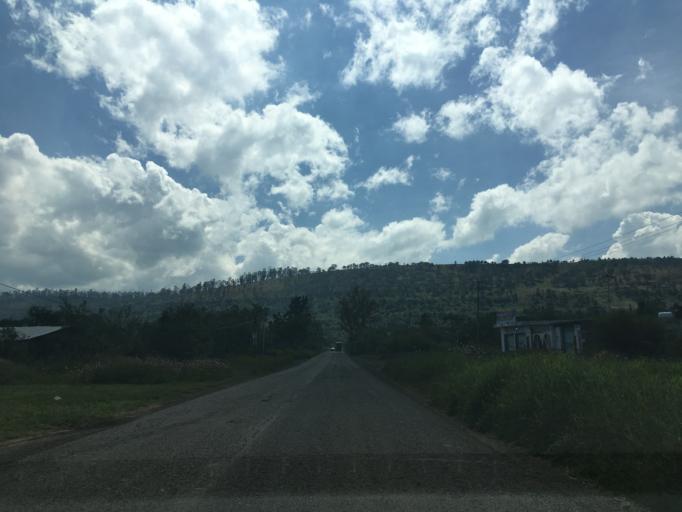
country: MX
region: Michoacan
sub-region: Morelia
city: La Mintzita (Piedra Dura)
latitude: 19.6460
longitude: -101.2795
